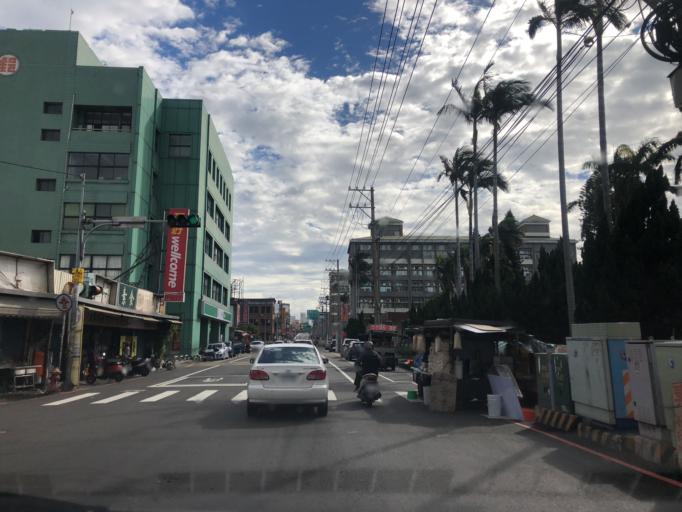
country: TW
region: Taiwan
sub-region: Hsinchu
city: Zhubei
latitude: 24.8400
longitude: 121.0025
